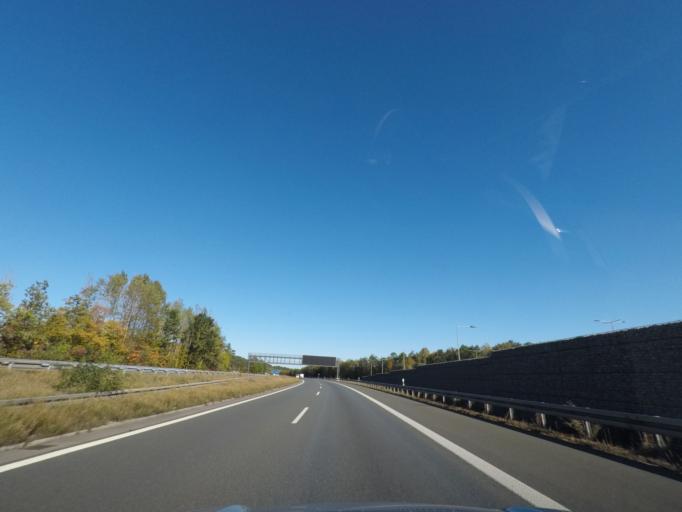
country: DE
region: Bavaria
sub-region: Regierungsbezirk Mittelfranken
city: Schnelldorf
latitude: 49.2048
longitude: 10.1981
